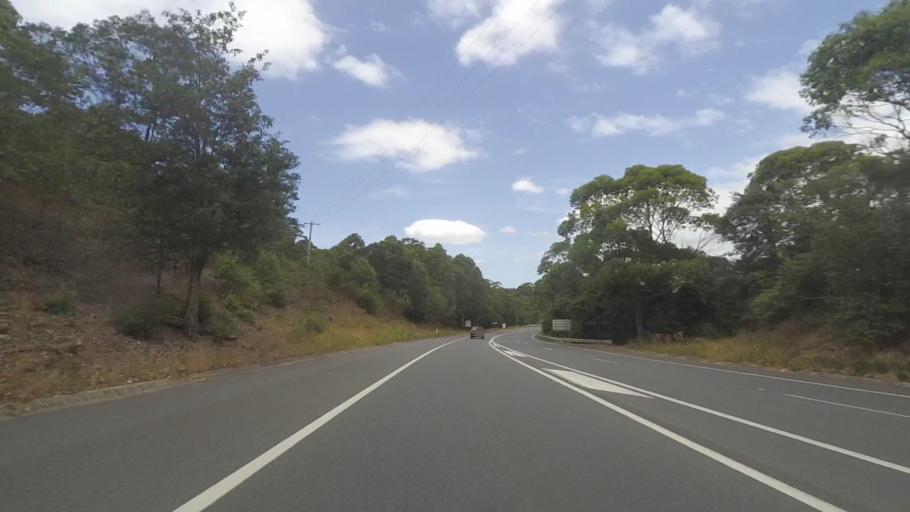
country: AU
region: New South Wales
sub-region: Shoalhaven Shire
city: Milton
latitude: -35.2606
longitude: 150.4281
